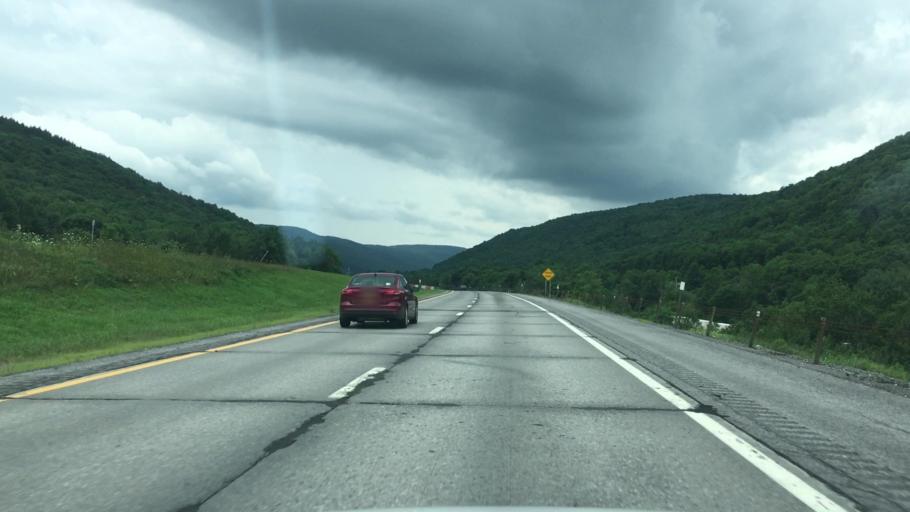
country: US
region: New York
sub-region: Otsego County
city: Worcester
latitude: 42.6441
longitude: -74.6471
